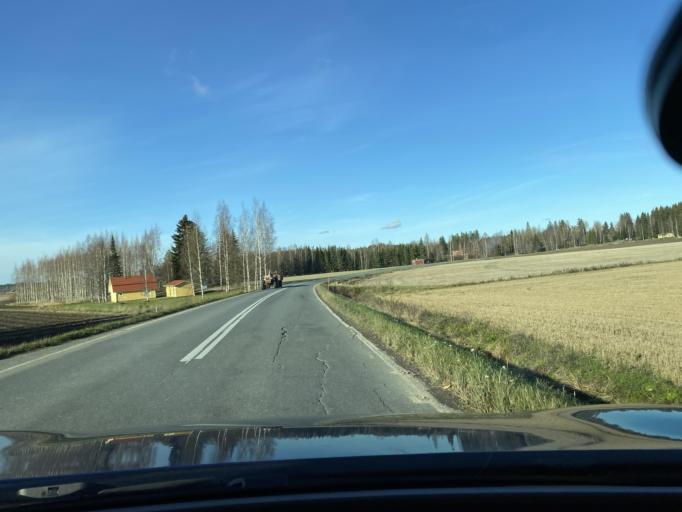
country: FI
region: Haeme
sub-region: Forssa
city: Tammela
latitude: 60.8393
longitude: 23.8345
